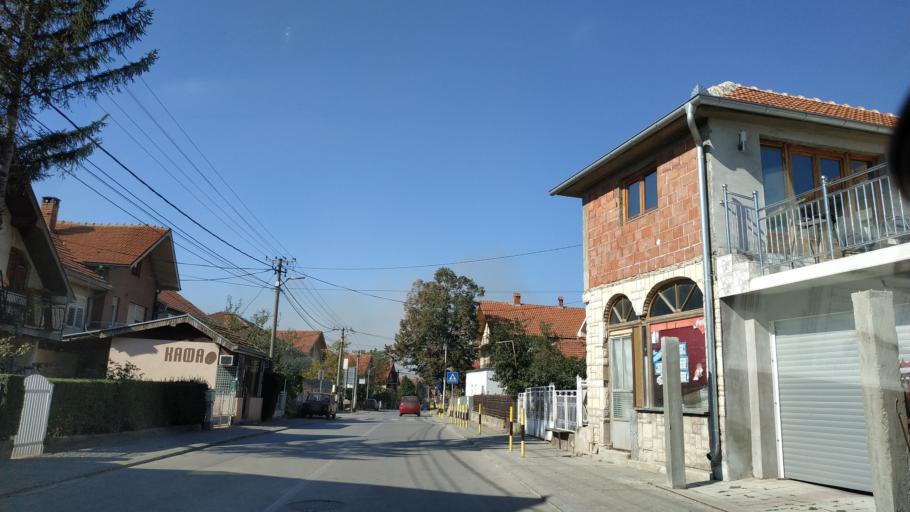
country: RS
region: Central Serbia
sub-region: Nisavski Okrug
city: Aleksinac
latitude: 43.5409
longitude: 21.6968
